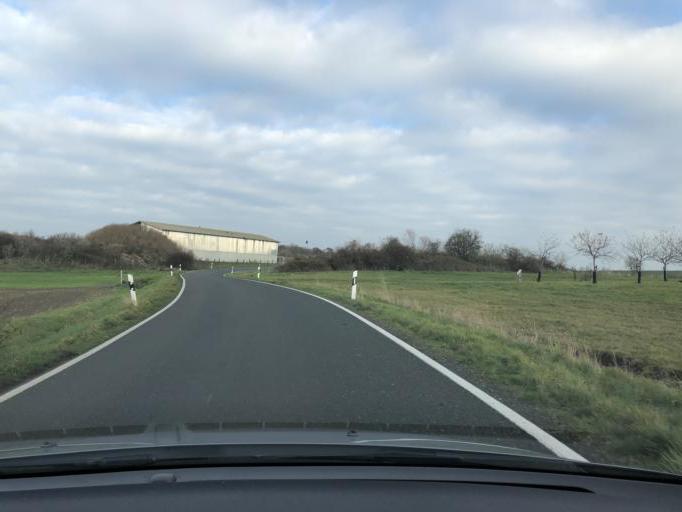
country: DE
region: Saxony
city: Nerchau
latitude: 51.2800
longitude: 12.8410
